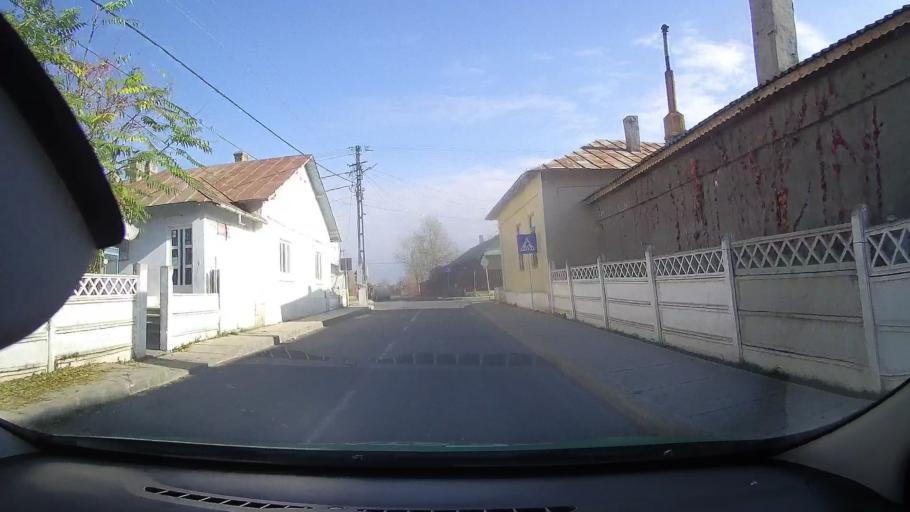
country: RO
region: Tulcea
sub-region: Comuna Murighiol
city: Murighiol
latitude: 45.0381
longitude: 29.1653
